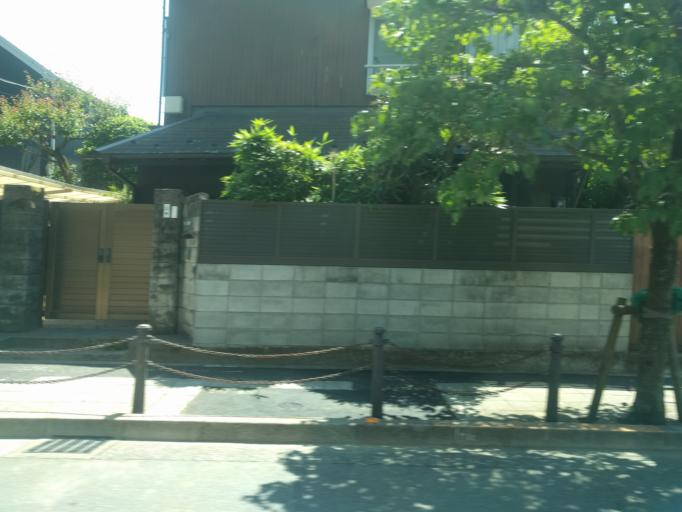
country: JP
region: Tokyo
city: Mitaka-shi
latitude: 35.6640
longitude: 139.6204
